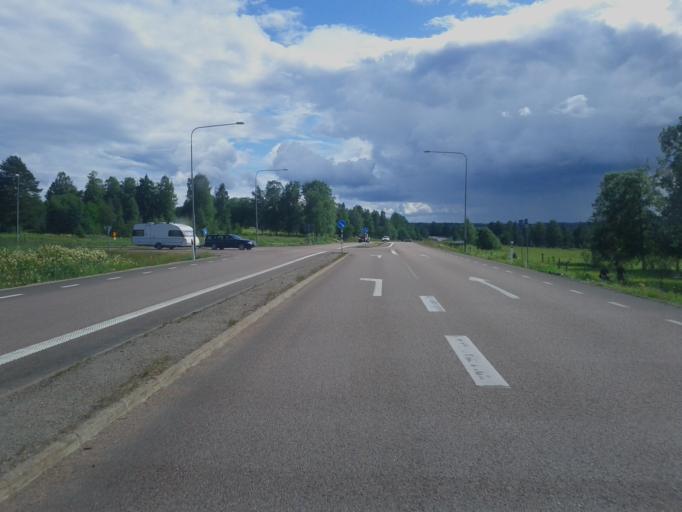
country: SE
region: Dalarna
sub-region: Rattviks Kommun
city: Raettvik
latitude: 60.8608
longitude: 15.1020
